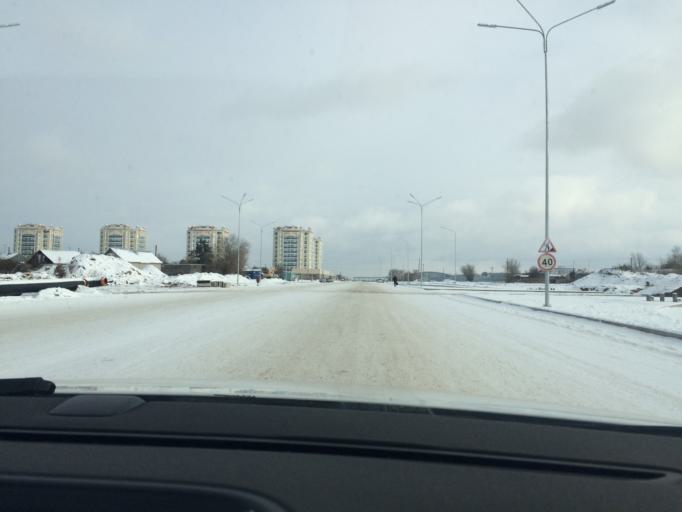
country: KZ
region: Astana Qalasy
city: Astana
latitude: 51.1201
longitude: 71.4983
